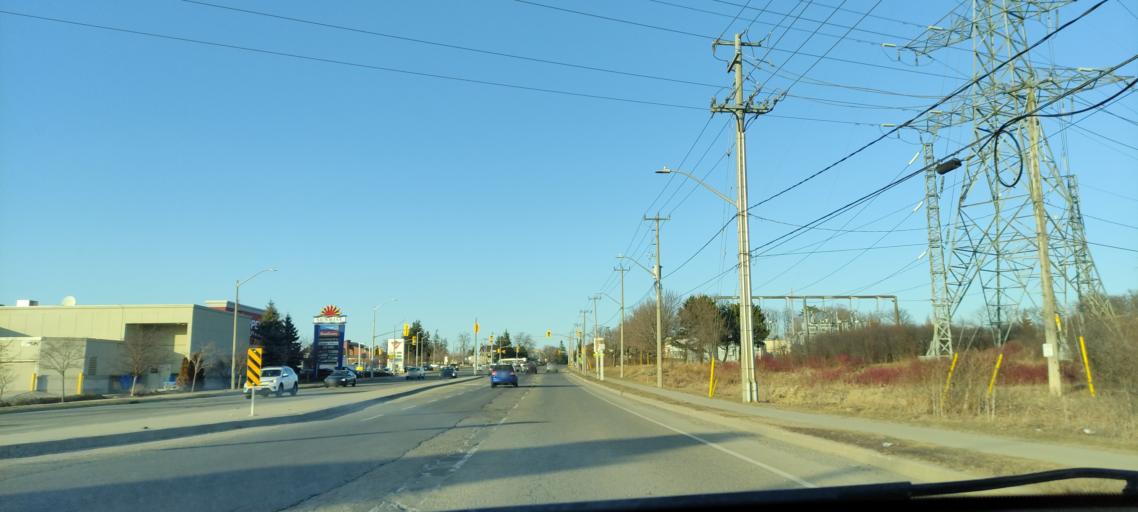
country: CA
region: Ontario
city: Kitchener
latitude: 43.4143
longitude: -80.5140
